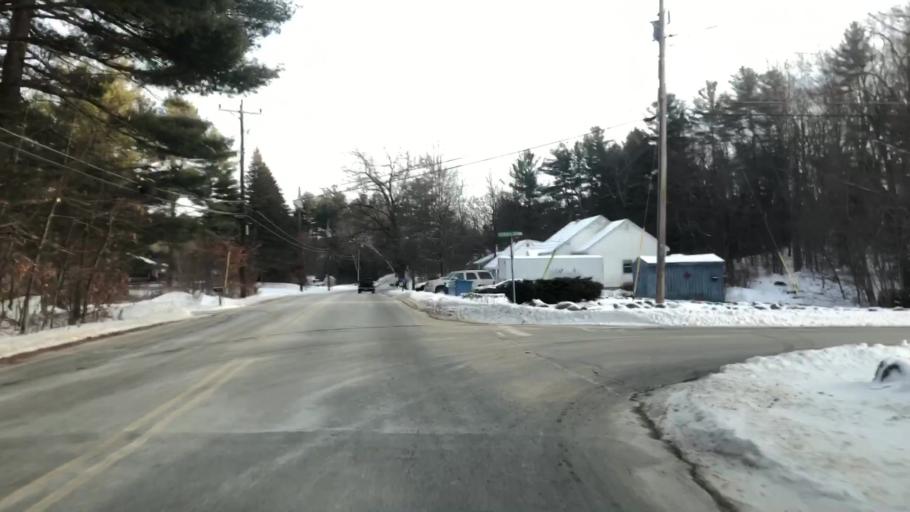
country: US
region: New Hampshire
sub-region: Hillsborough County
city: Wilton
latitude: 42.8285
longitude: -71.7008
